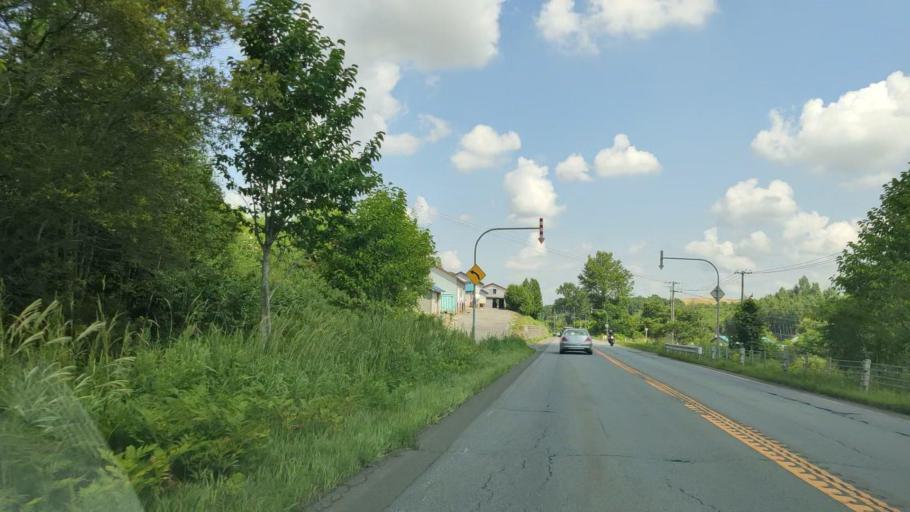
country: JP
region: Hokkaido
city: Shimo-furano
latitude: 43.5586
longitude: 142.4349
